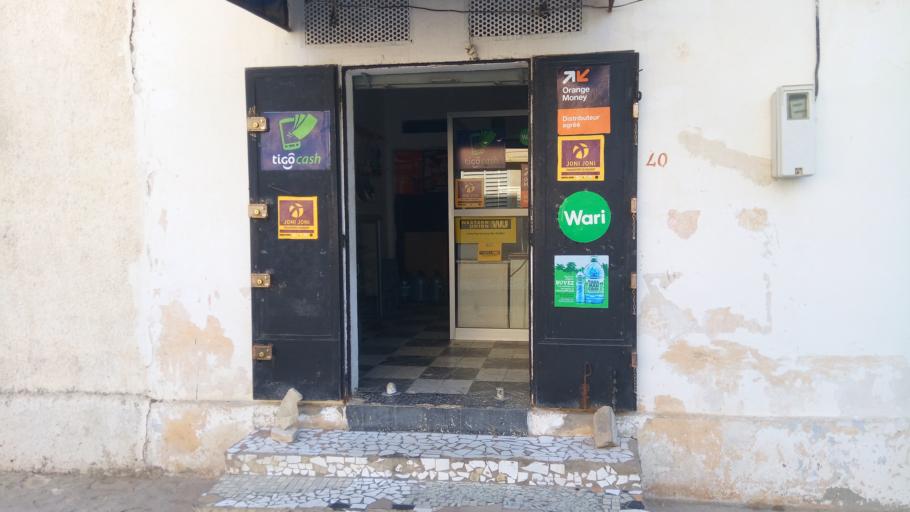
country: SN
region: Dakar
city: Dakar
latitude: 14.6802
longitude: -17.4630
